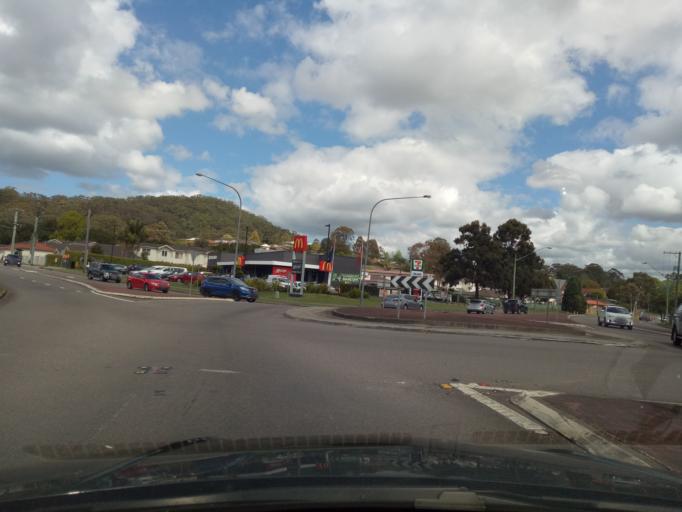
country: AU
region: New South Wales
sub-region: Gosford Shire
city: Lisarow
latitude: -33.3849
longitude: 151.3666
